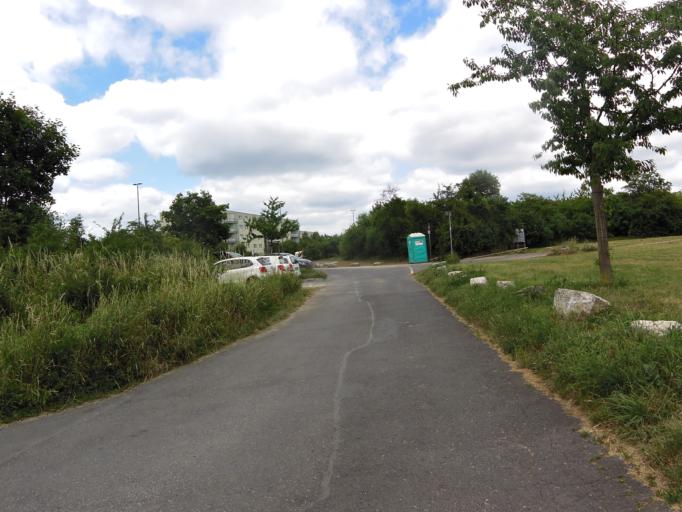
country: DE
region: Bavaria
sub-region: Regierungsbezirk Unterfranken
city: Wuerzburg
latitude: 49.7778
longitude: 9.9672
